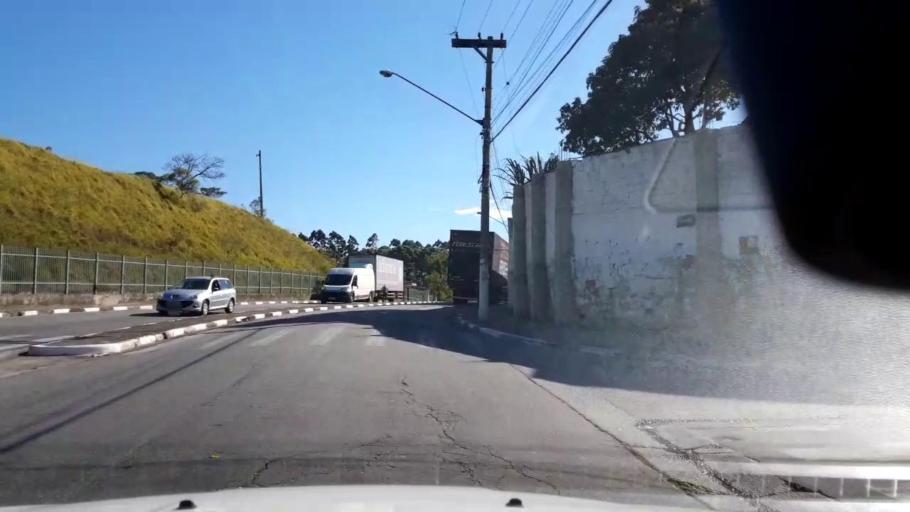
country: BR
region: Sao Paulo
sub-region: Ferraz De Vasconcelos
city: Ferraz de Vasconcelos
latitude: -23.5357
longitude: -46.3900
